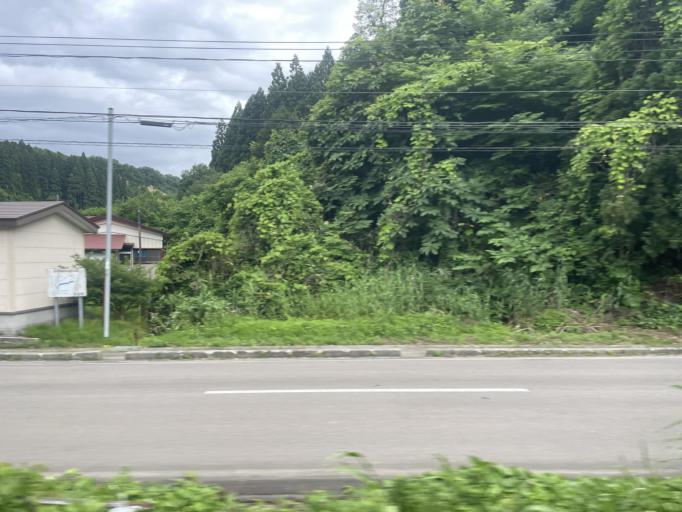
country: JP
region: Akita
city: Tenno
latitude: 39.9124
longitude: 139.8837
